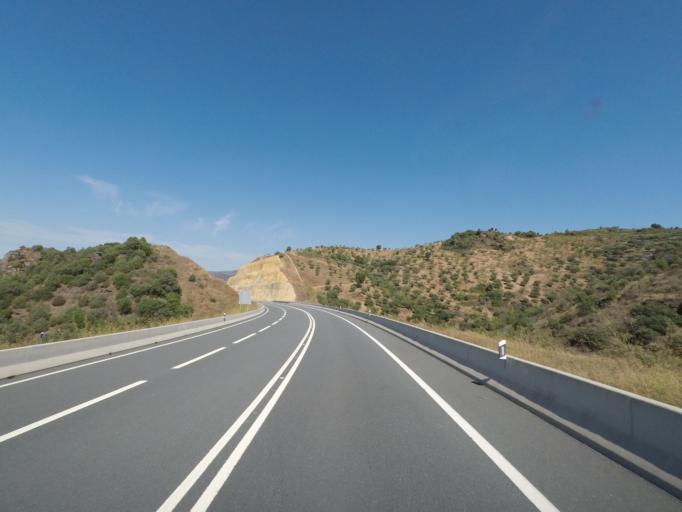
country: PT
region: Braganca
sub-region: Alfandega da Fe
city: Alfandega da Fe
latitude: 41.2944
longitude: -6.8962
